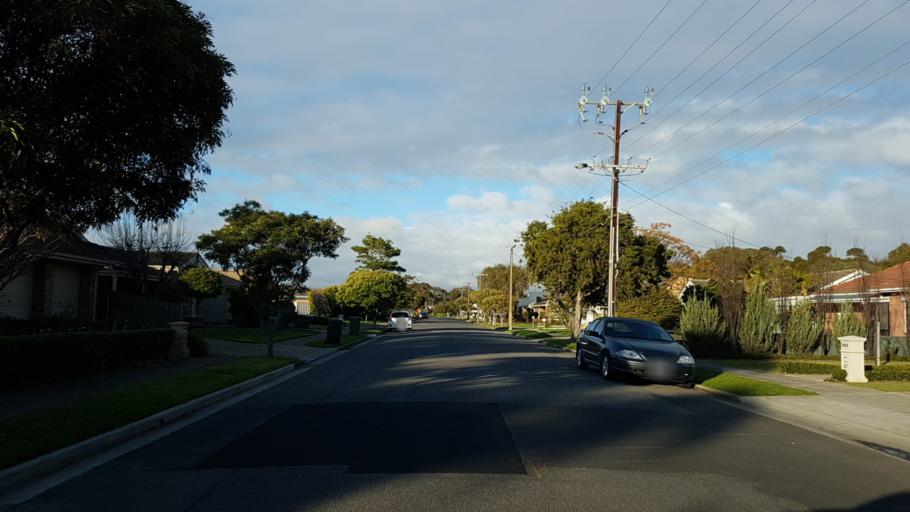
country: AU
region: South Australia
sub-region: Charles Sturt
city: Henley Beach
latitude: -34.9314
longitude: 138.5135
